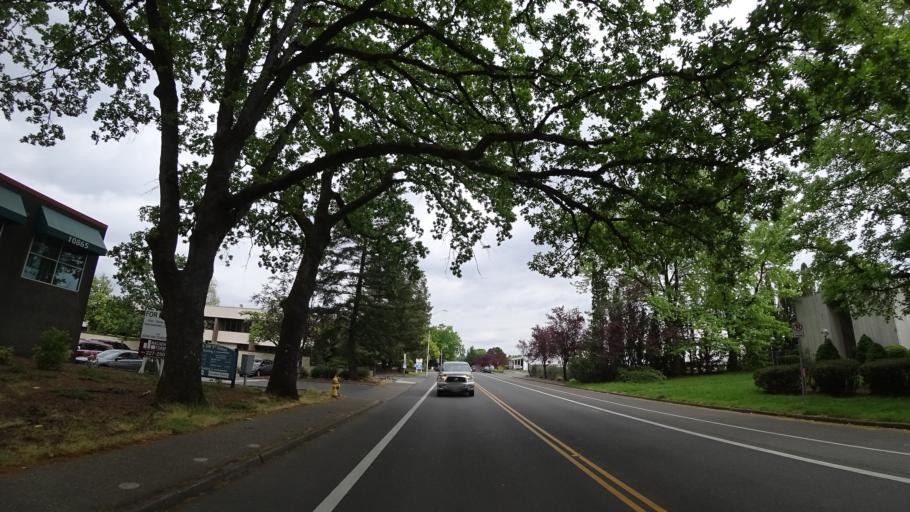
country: US
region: Oregon
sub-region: Washington County
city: Beaverton
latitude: 45.4838
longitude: -122.7884
